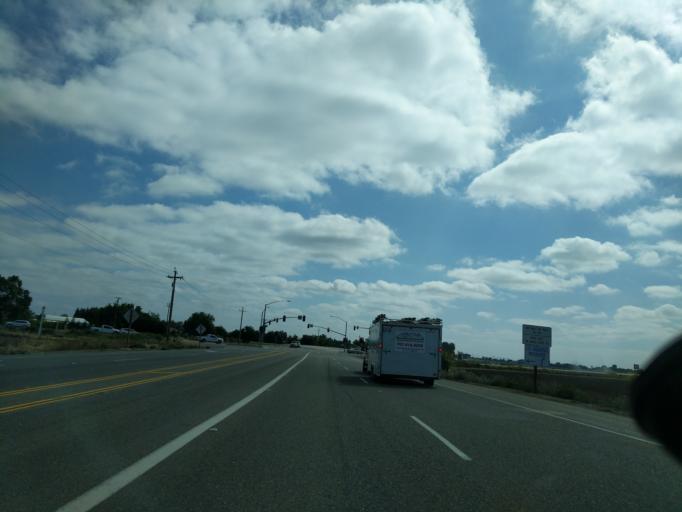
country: US
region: California
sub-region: Contra Costa County
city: Brentwood
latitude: 37.8953
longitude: -121.7142
